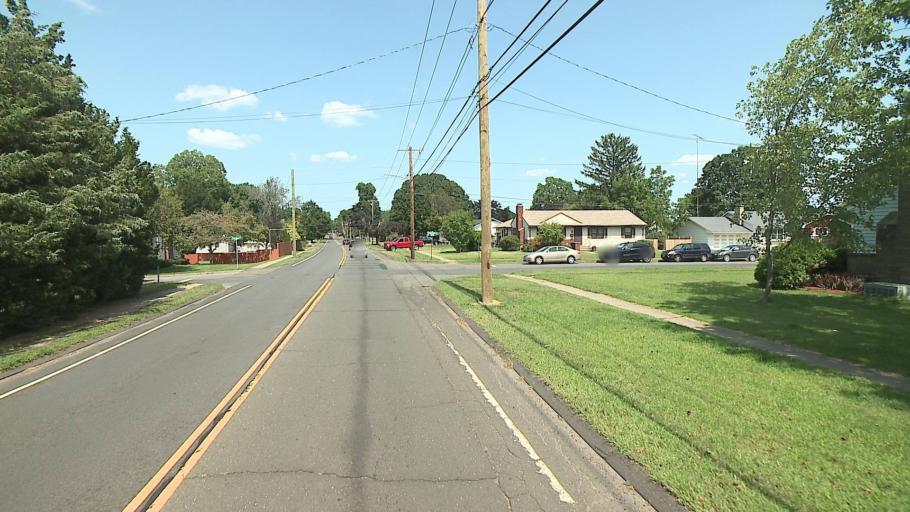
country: US
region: Connecticut
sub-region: Fairfield County
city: Stratford
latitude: 41.2147
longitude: -73.1192
